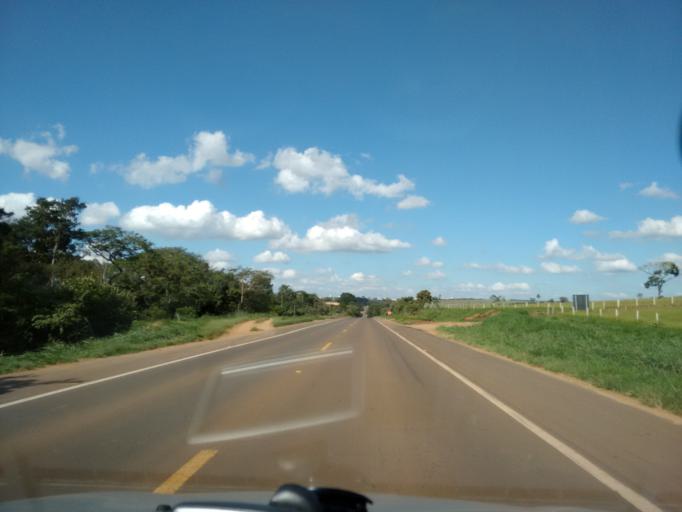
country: BR
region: Sao Paulo
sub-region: Sao Carlos
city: Sao Carlos
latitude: -22.0651
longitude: -47.9242
